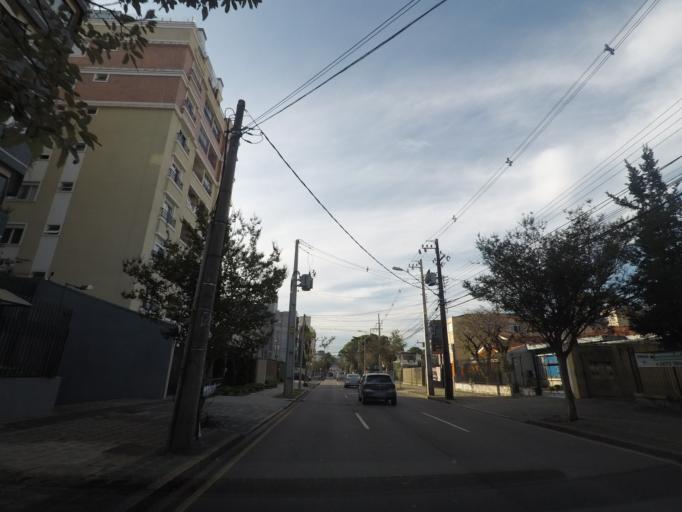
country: BR
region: Parana
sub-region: Curitiba
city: Curitiba
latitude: -25.4215
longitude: -49.2530
